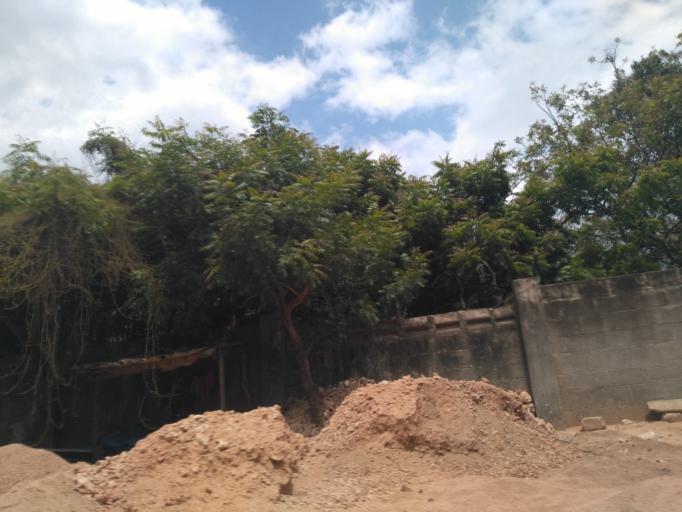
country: TZ
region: Dar es Salaam
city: Magomeni
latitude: -6.7616
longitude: 39.2728
